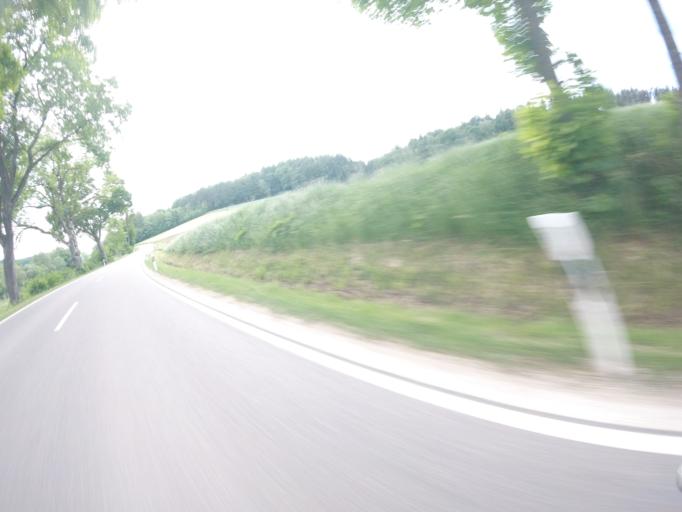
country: DE
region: Bavaria
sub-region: Upper Bavaria
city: Reichertshausen
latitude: 48.4832
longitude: 11.5262
